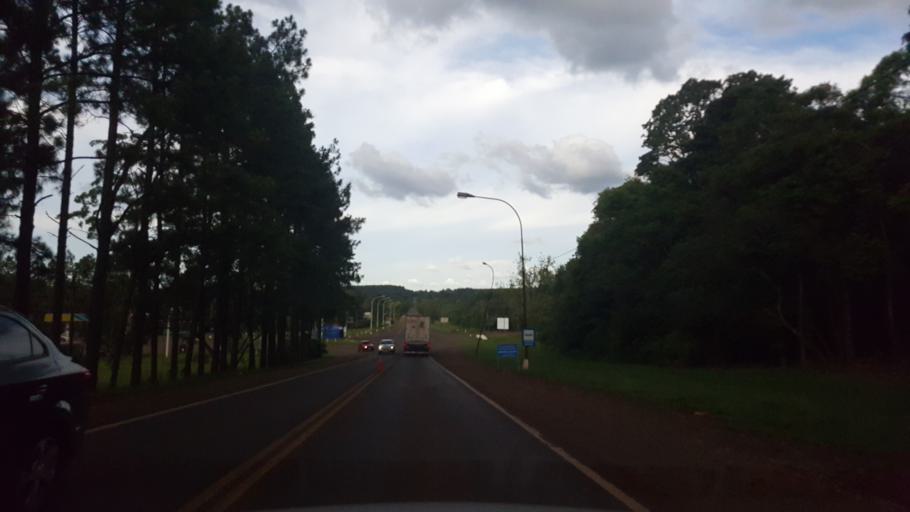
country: AR
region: Misiones
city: Gobernador Roca
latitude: -27.1800
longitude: -55.4576
